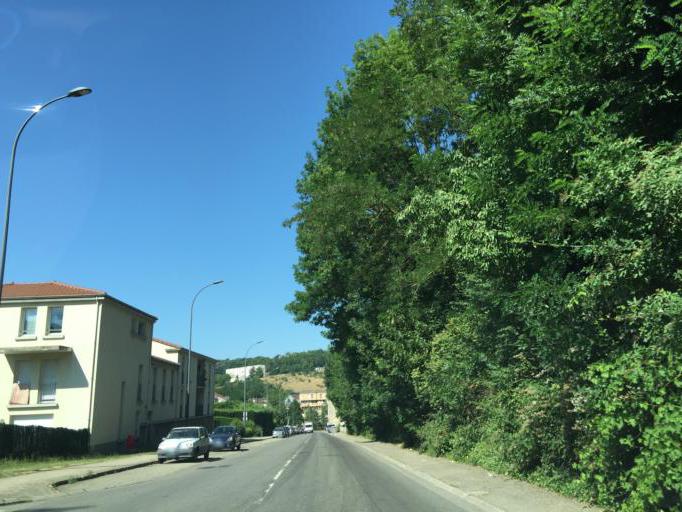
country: FR
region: Rhone-Alpes
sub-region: Departement de la Loire
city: Saint-Jean-Bonnefonds
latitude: 45.4323
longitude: 4.4348
